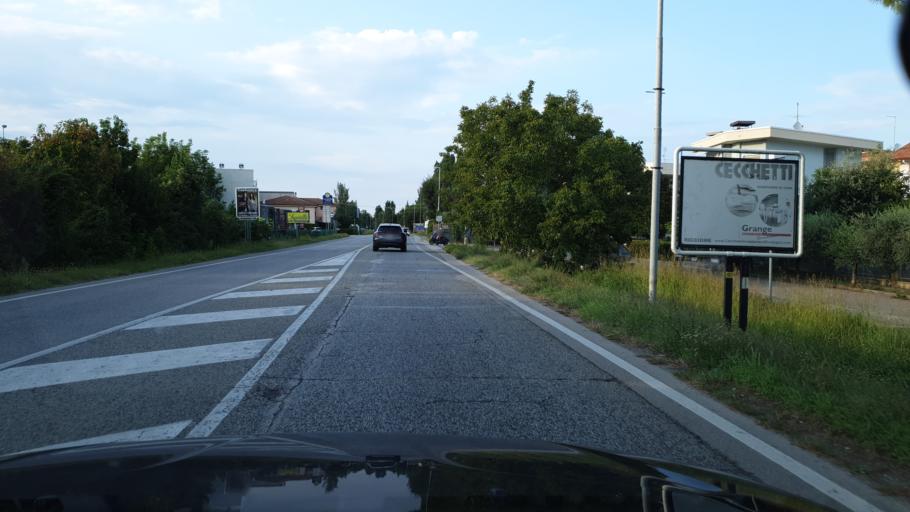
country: IT
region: Emilia-Romagna
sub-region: Provincia di Rimini
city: Riccione
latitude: 44.0094
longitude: 12.6333
